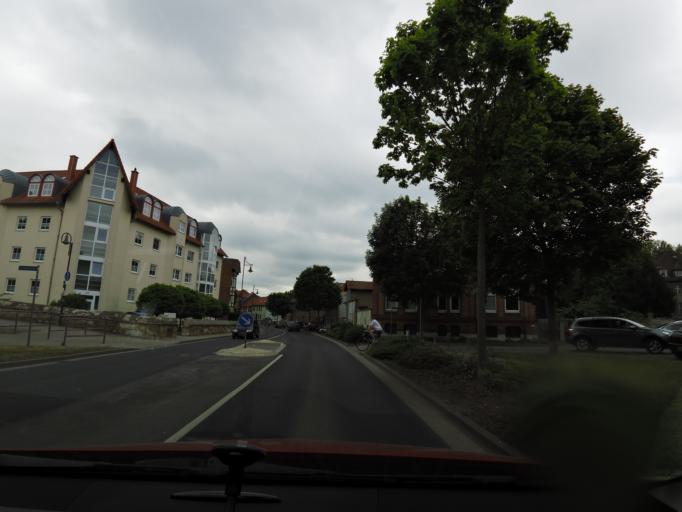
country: DE
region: Thuringia
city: Muehlhausen
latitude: 51.2057
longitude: 10.4524
